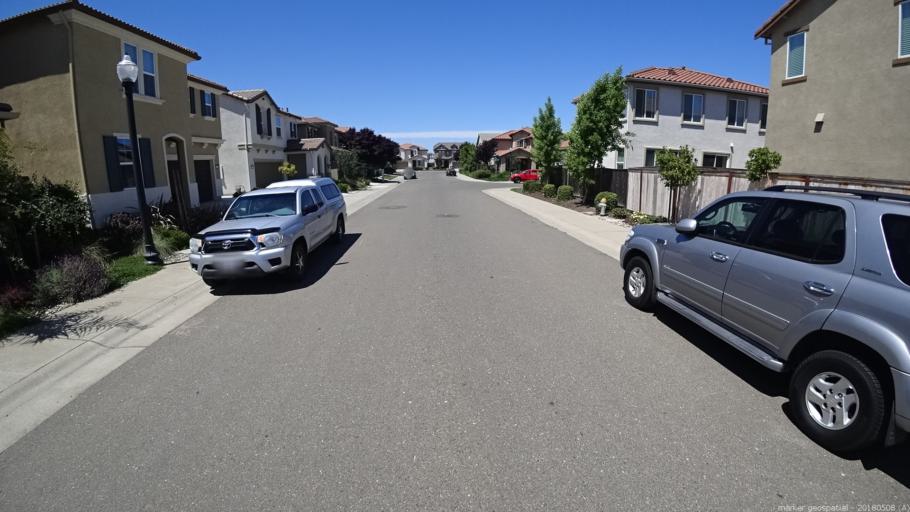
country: US
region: California
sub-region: Sacramento County
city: Elverta
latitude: 38.6722
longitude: -121.5313
